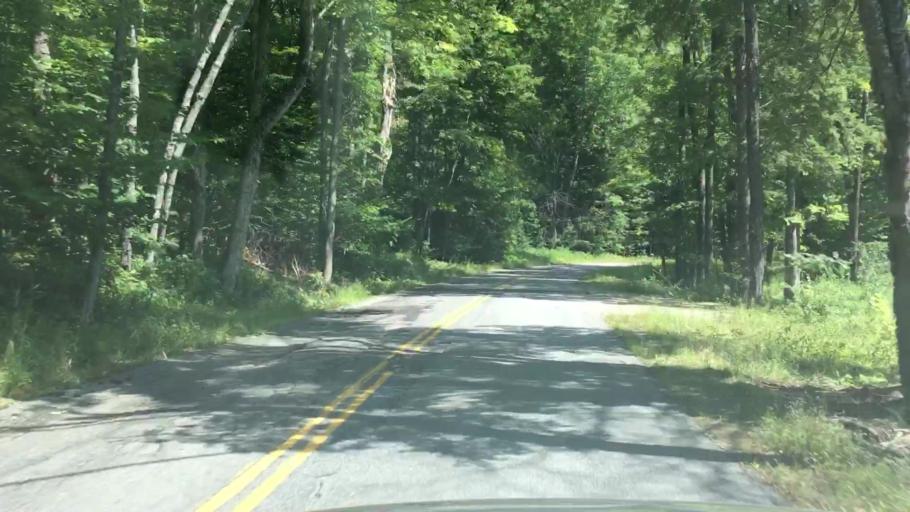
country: US
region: Vermont
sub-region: Windham County
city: West Brattleboro
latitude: 42.8052
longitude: -72.7086
